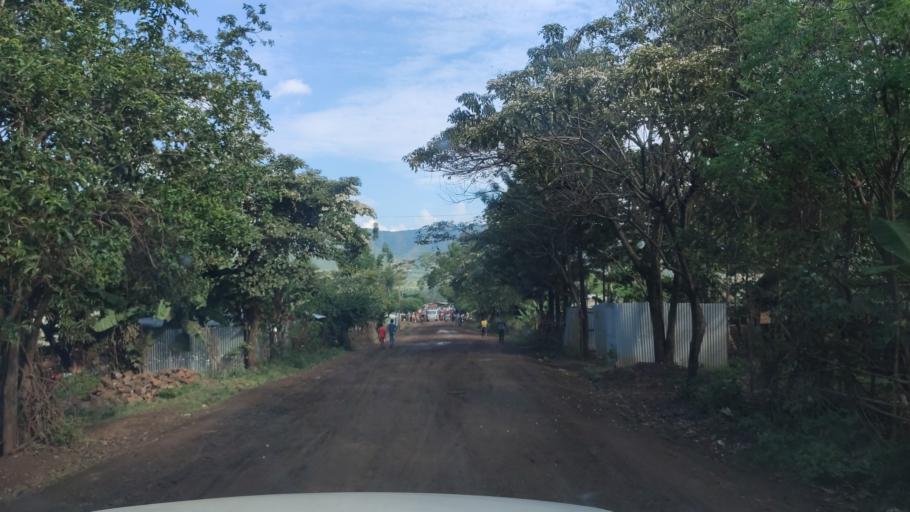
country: ET
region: Southern Nations, Nationalities, and People's Region
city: Felege Neway
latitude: 6.4259
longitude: 37.3075
